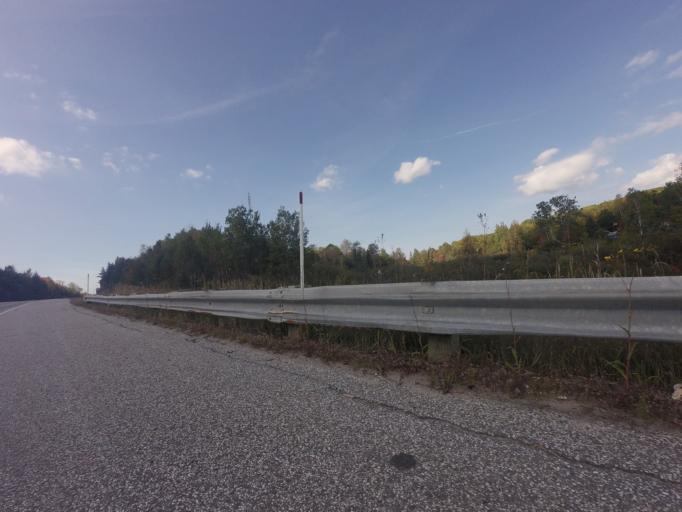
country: CA
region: Quebec
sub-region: Laurentides
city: Mont-Laurier
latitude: 46.5589
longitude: -75.6991
